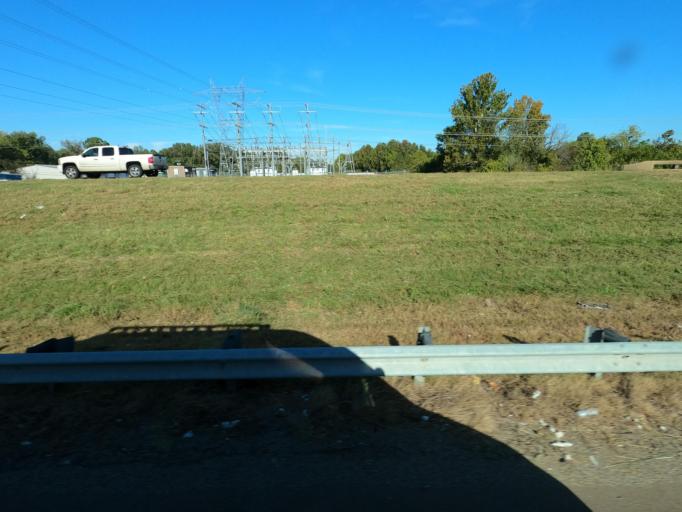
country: US
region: Tennessee
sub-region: Tipton County
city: Munford
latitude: 35.4103
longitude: -89.8323
